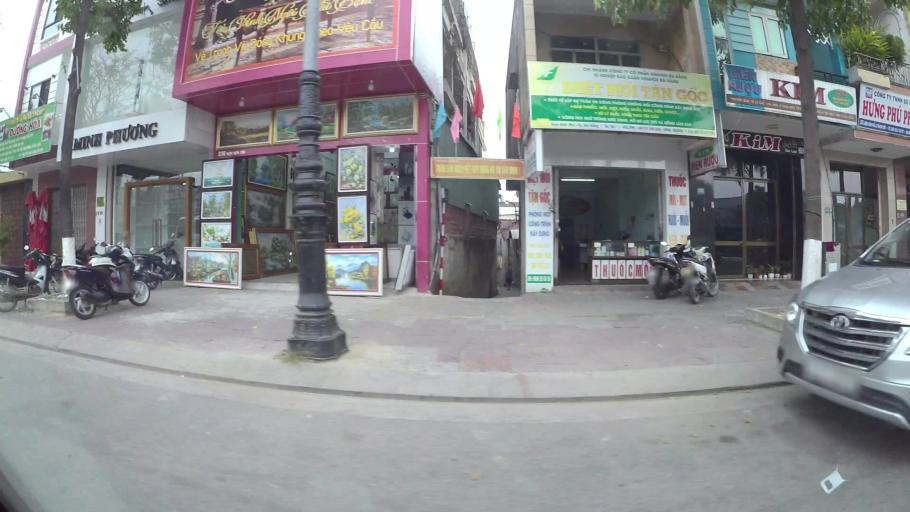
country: VN
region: Da Nang
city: Thanh Khe
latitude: 16.0659
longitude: 108.1959
